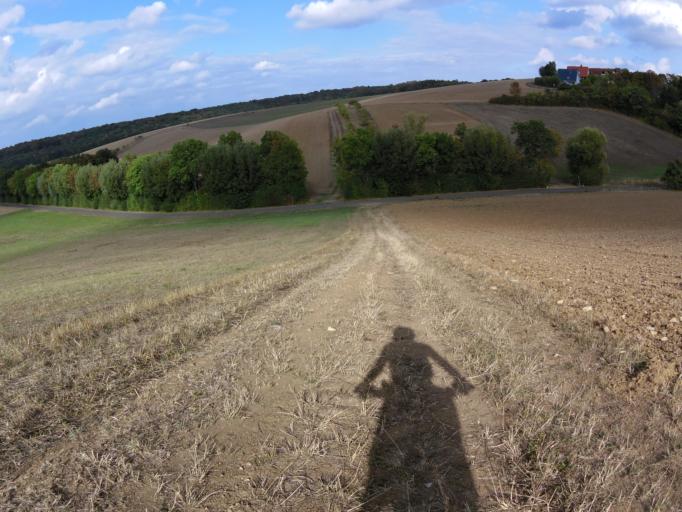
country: DE
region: Bavaria
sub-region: Regierungsbezirk Unterfranken
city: Eisingen
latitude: 49.7626
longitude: 9.8199
